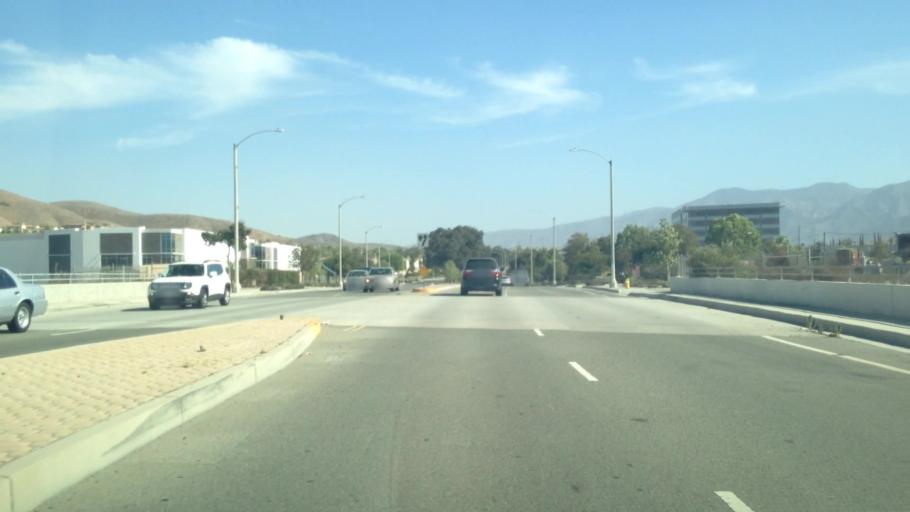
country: US
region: California
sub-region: Riverside County
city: El Cerrito
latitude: 33.8228
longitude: -117.5096
